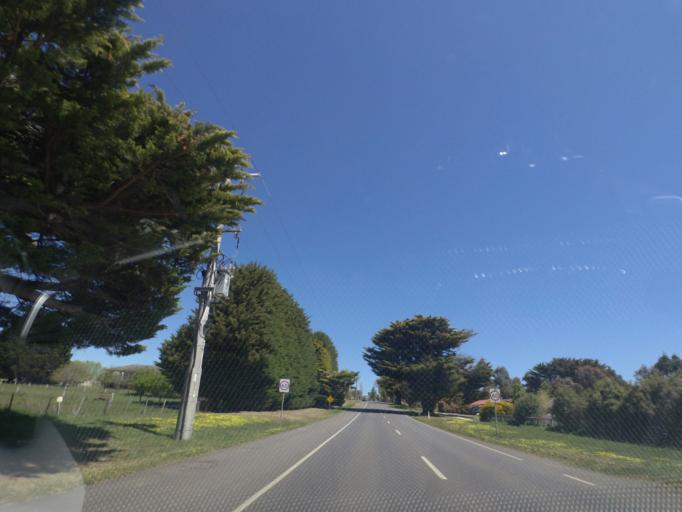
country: AU
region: Victoria
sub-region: Hume
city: Sunbury
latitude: -37.2775
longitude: 144.7398
